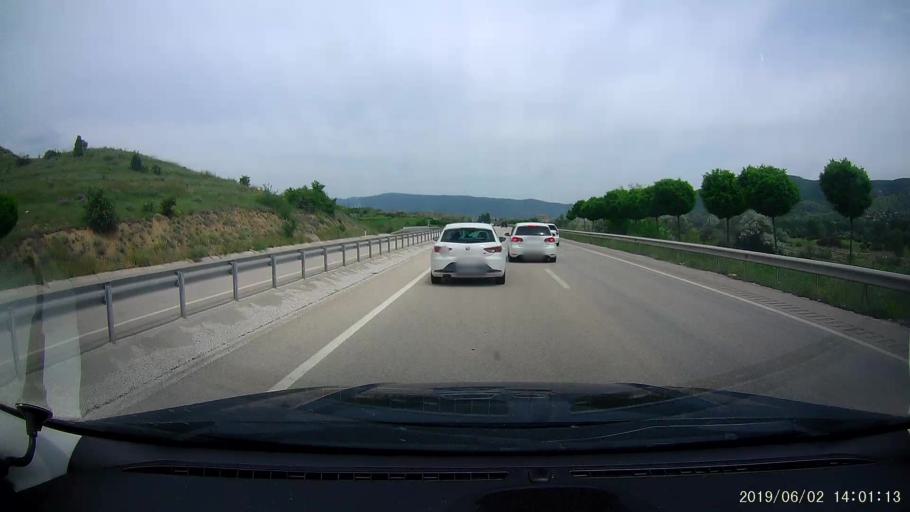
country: TR
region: Cankiri
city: Ilgaz
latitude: 40.9068
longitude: 33.5877
